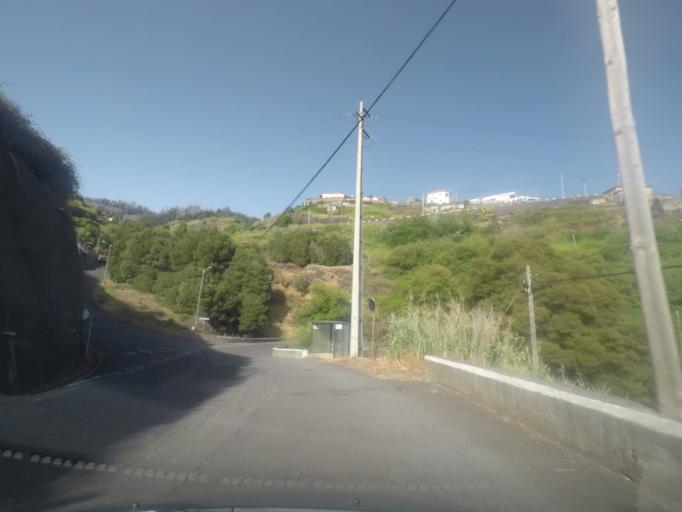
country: PT
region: Madeira
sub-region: Calheta
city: Estreito da Calheta
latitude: 32.7304
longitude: -17.1691
